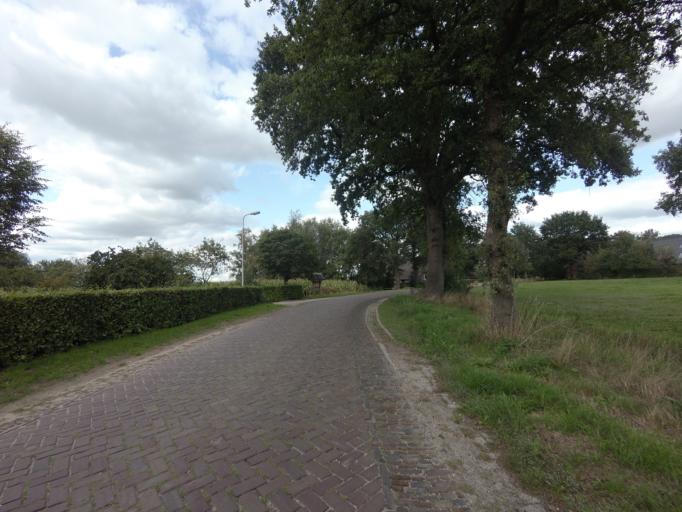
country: NL
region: Drenthe
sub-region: Gemeente De Wolden
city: Ruinen
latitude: 52.7465
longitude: 6.3633
